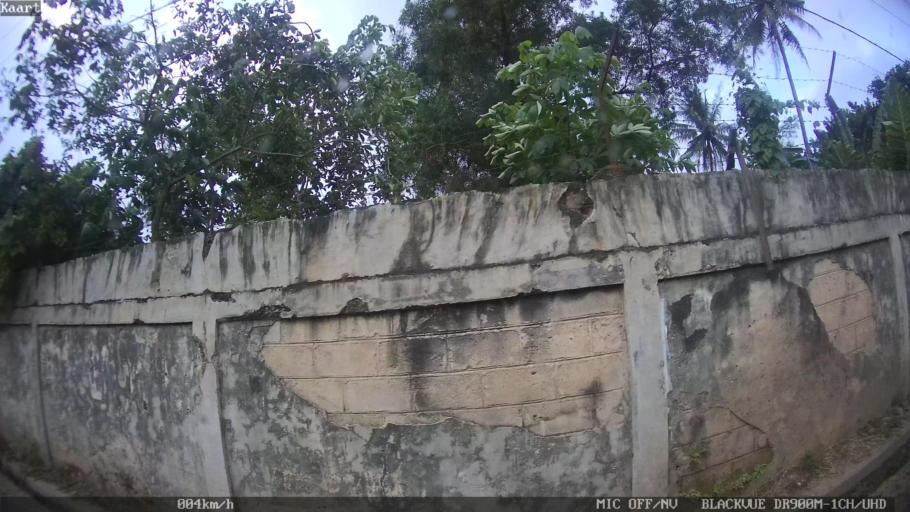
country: ID
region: Lampung
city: Bandarlampung
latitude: -5.4117
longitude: 105.2943
